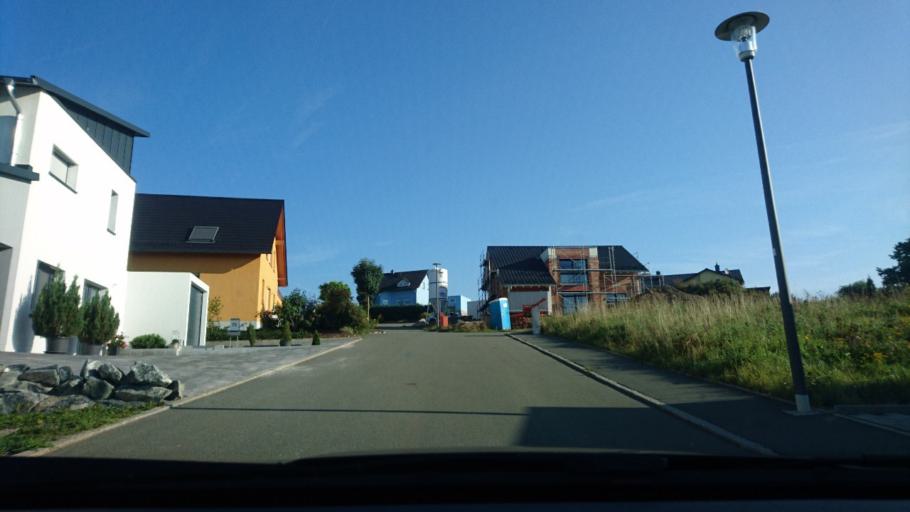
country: DE
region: Bavaria
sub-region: Upper Franconia
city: Naila
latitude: 50.3335
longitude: 11.6919
